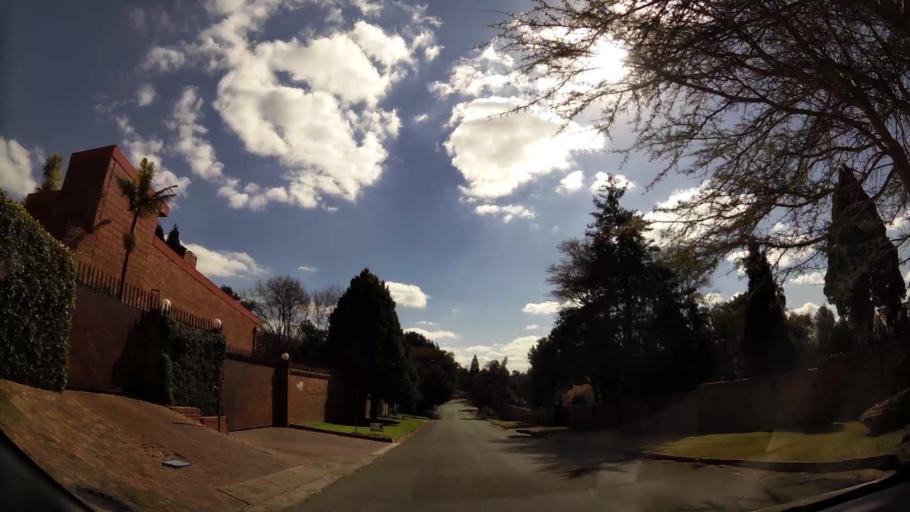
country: ZA
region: Gauteng
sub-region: West Rand District Municipality
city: Krugersdorp
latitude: -26.0874
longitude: 27.7953
